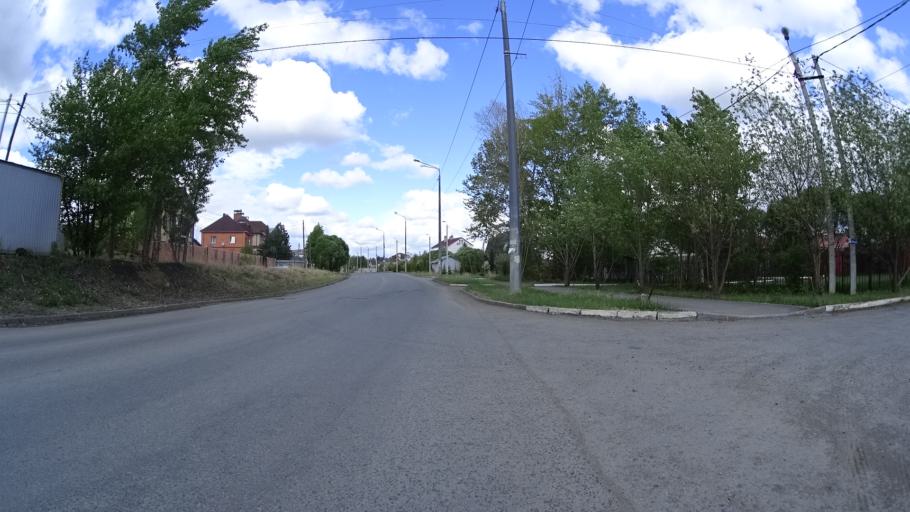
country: RU
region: Chelyabinsk
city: Sargazy
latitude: 55.1522
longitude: 61.2734
